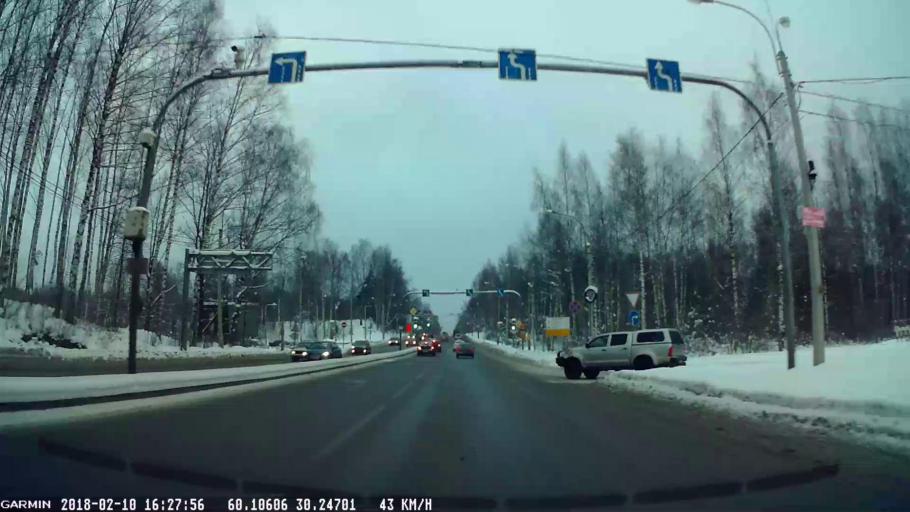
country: RU
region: St.-Petersburg
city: Pargolovo
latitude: 60.1063
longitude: 30.2468
